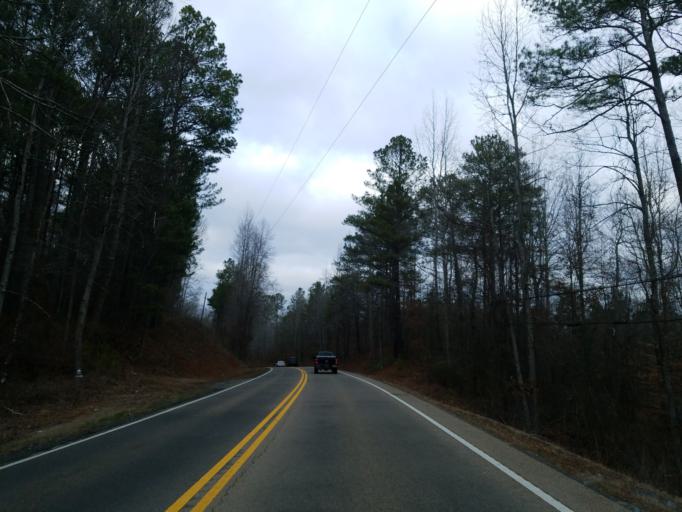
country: US
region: Georgia
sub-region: Cherokee County
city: Canton
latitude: 34.2953
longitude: -84.5179
